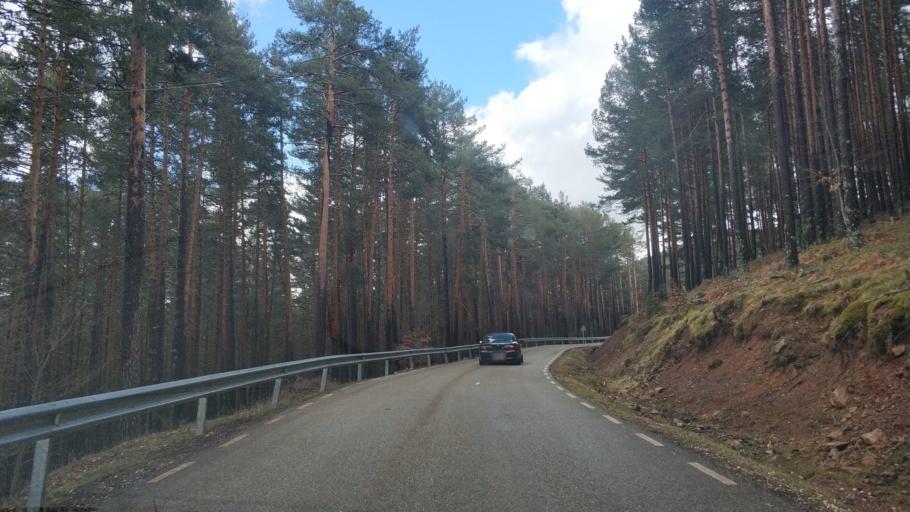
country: ES
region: Castille and Leon
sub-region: Provincia de Burgos
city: Neila
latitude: 42.0477
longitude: -3.0119
